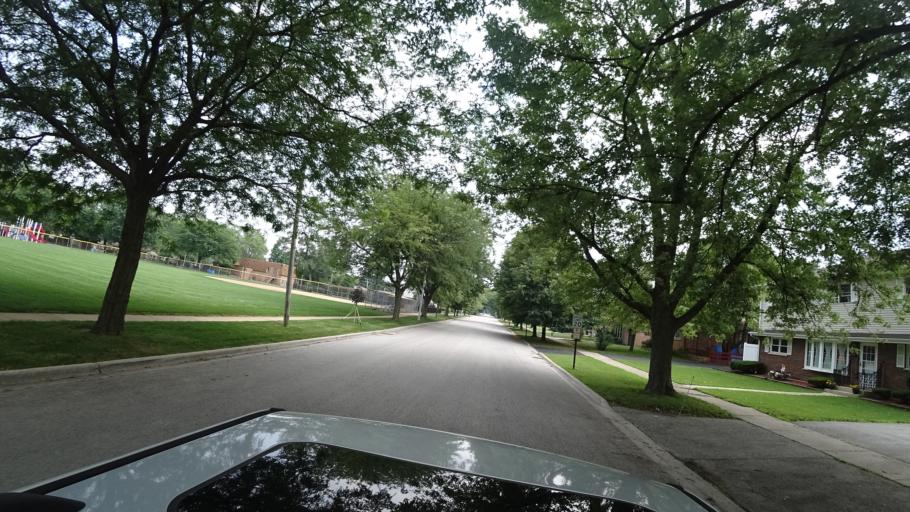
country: US
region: Illinois
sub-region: Cook County
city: Chicago Ridge
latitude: 41.6974
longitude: -87.7754
